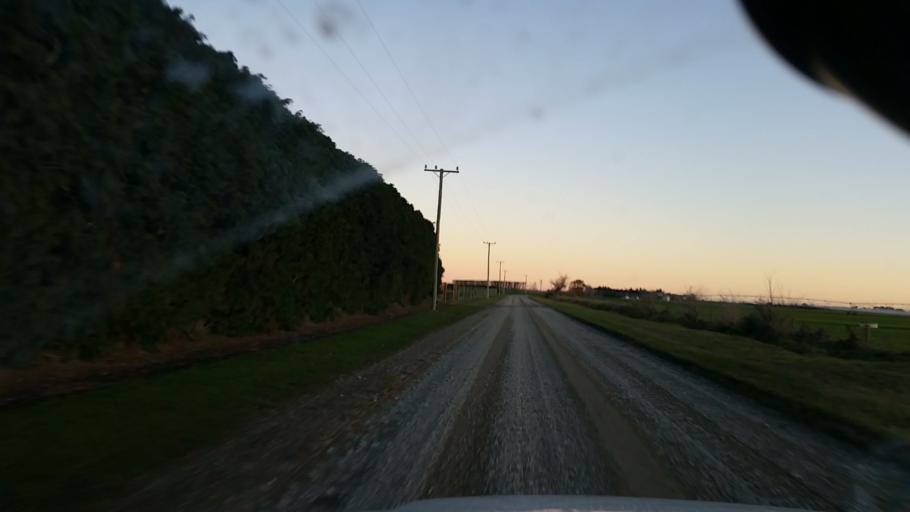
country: NZ
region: Canterbury
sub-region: Ashburton District
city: Tinwald
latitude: -44.0505
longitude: 171.6630
